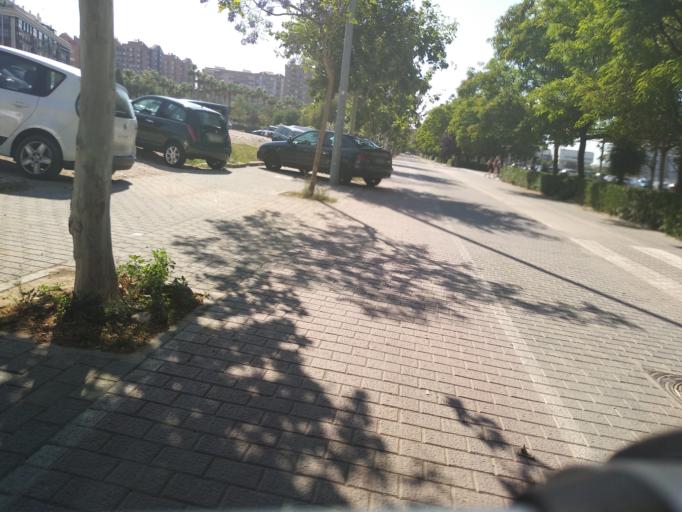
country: ES
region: Valencia
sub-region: Provincia de Valencia
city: Alboraya
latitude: 39.4785
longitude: -0.3476
